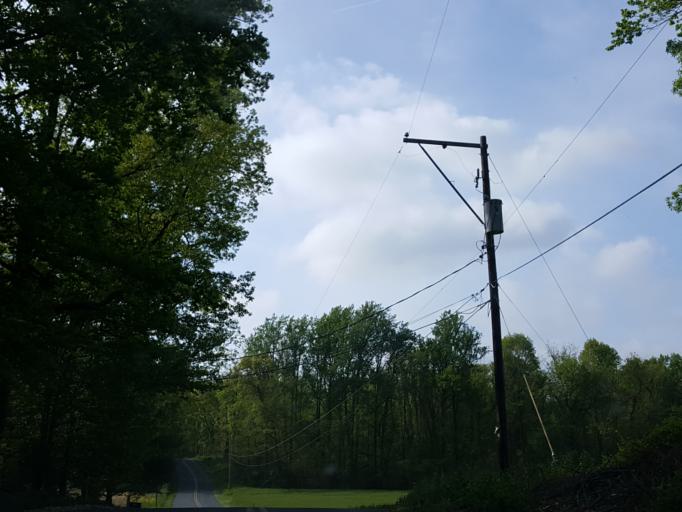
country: US
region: Pennsylvania
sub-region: Lancaster County
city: Elizabethtown
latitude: 40.1852
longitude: -76.5575
